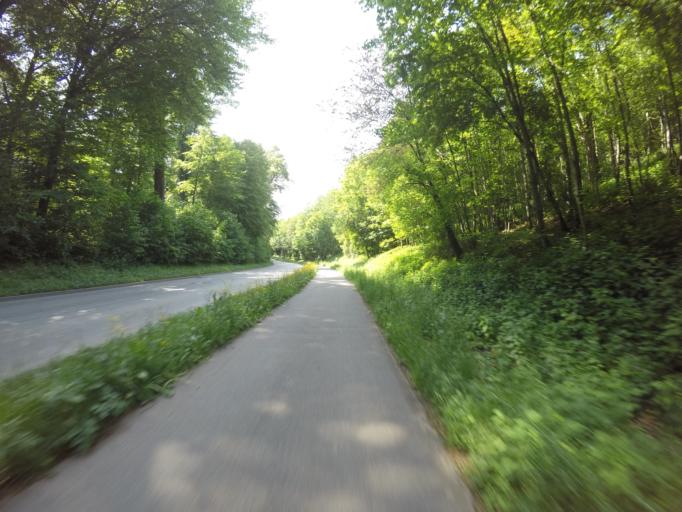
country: DE
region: Baden-Wuerttemberg
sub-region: Tuebingen Region
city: Kusterdingen
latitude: 48.5110
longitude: 9.0939
